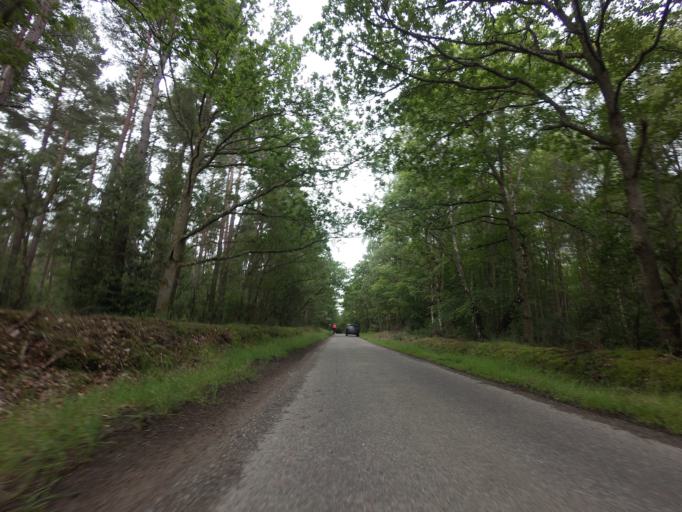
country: GB
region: Scotland
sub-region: Moray
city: Forres
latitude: 57.6179
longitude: -3.6772
